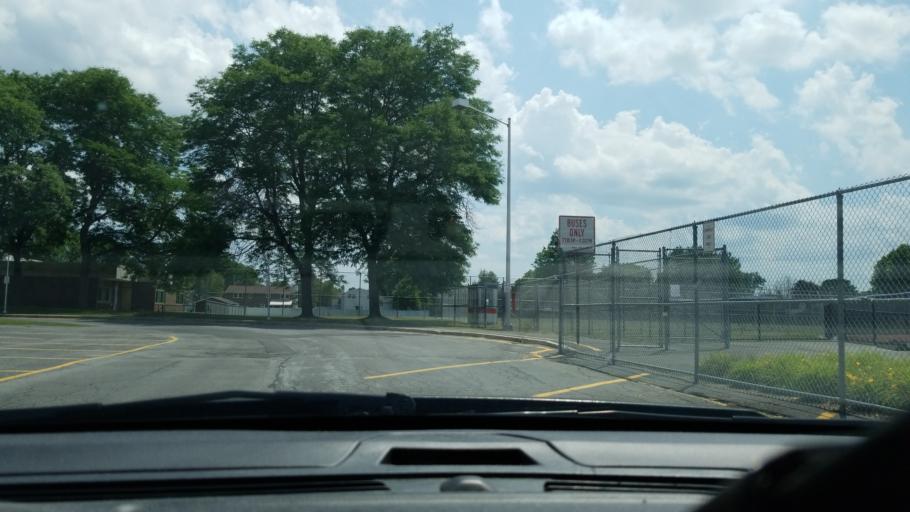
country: US
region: New York
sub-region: Onondaga County
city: Liverpool
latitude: 43.1482
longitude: -76.2116
